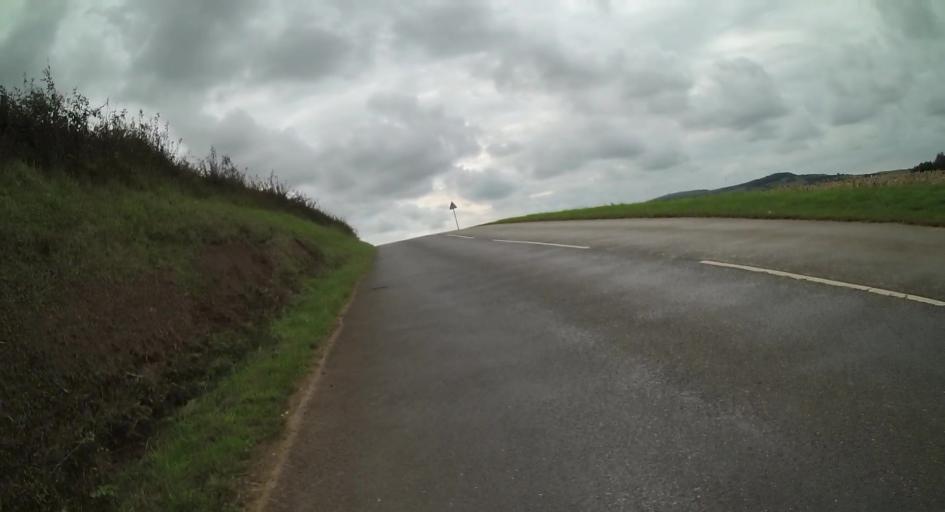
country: GB
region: England
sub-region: Isle of Wight
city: Niton
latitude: 50.6276
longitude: -1.2639
